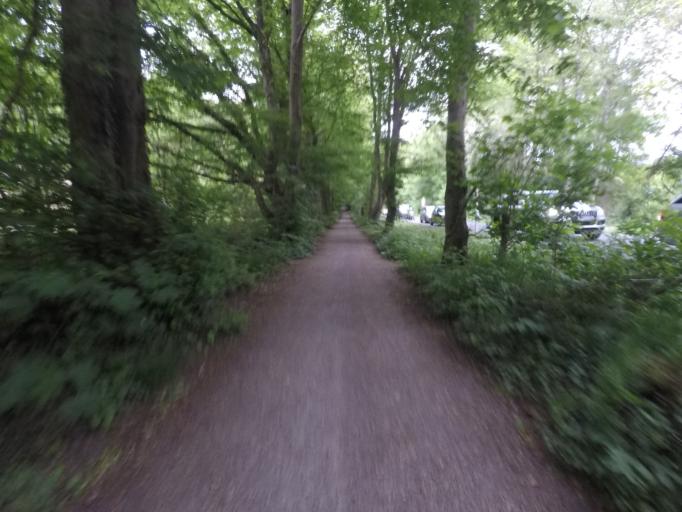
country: DE
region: North Rhine-Westphalia
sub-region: Regierungsbezirk Detmold
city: Bad Salzuflen
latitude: 52.1002
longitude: 8.7557
